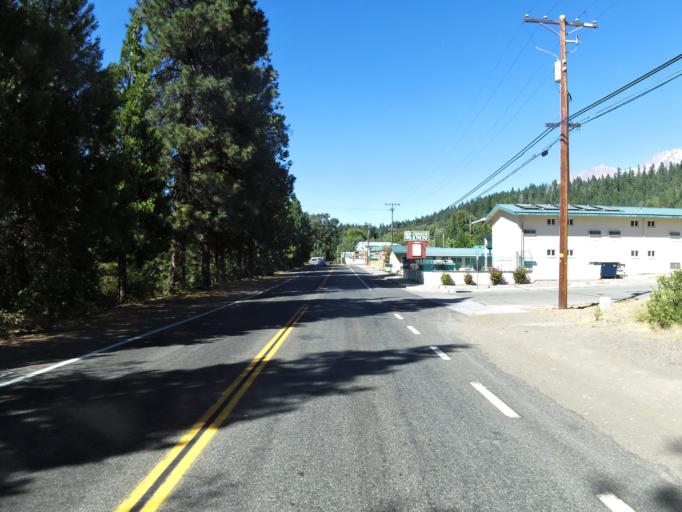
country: US
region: California
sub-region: Siskiyou County
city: Mount Shasta
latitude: 41.3002
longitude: -122.3062
